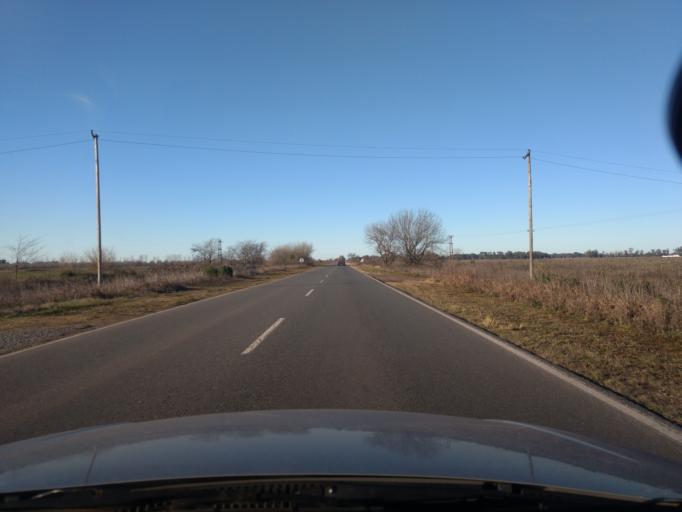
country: AR
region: Buenos Aires
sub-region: Partido de Lujan
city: Lujan
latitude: -34.6332
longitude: -59.1083
